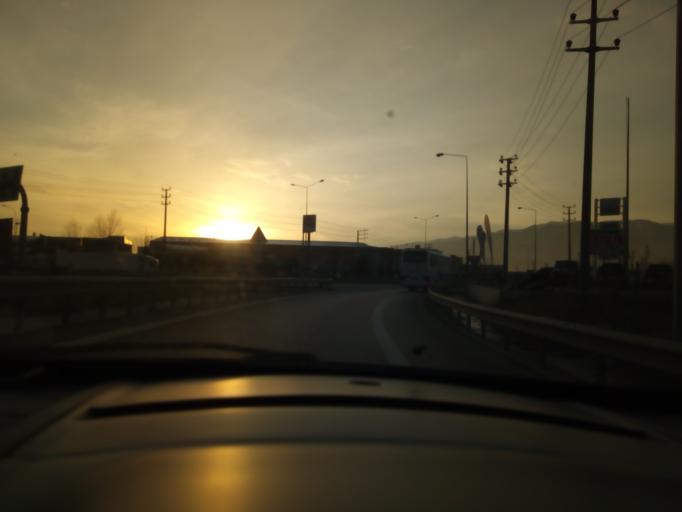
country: TR
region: Bursa
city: Demirtas
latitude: 40.2741
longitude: 29.0531
